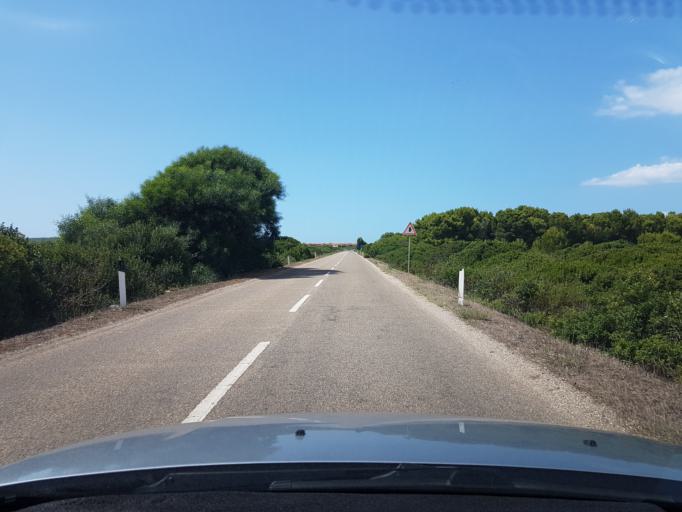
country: IT
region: Sardinia
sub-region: Provincia di Oristano
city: Riola Sardo
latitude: 40.0349
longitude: 8.4224
